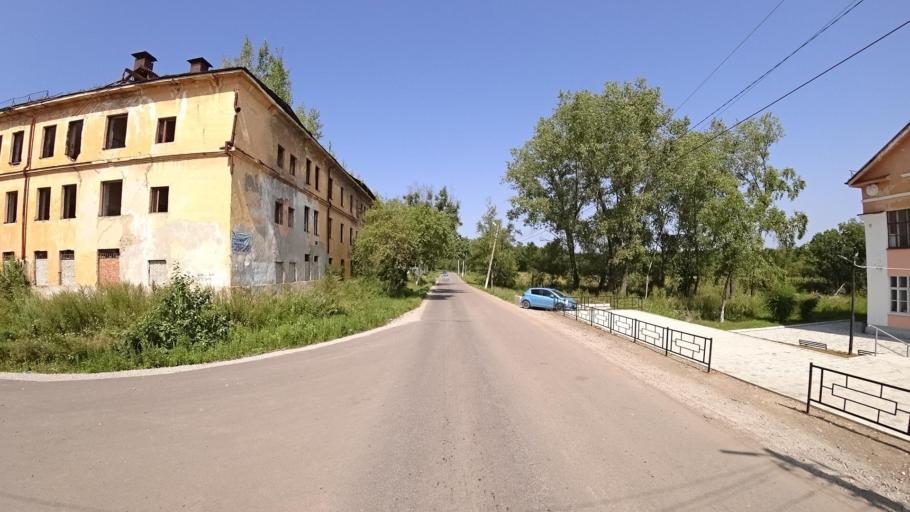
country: RU
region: Khabarovsk Krai
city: Khor
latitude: 47.9685
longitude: 135.1167
